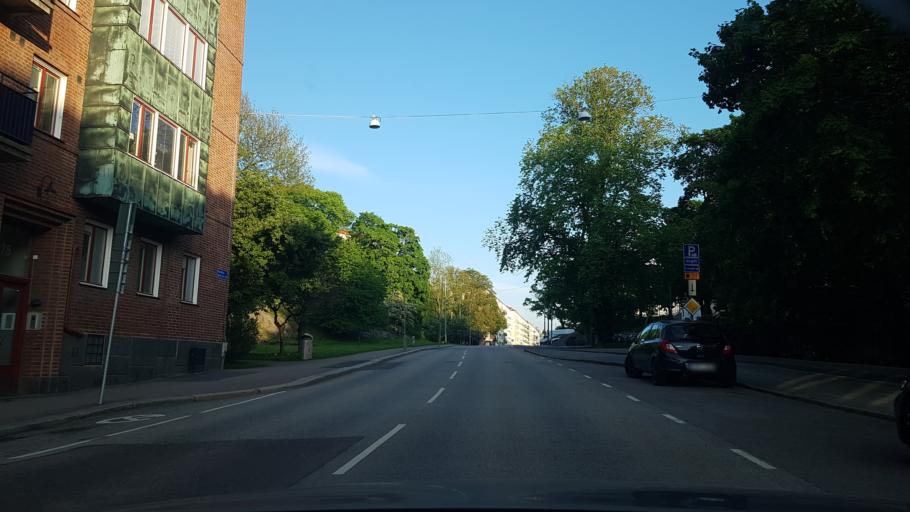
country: SE
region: Vaestra Goetaland
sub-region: Goteborg
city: Goeteborg
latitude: 57.6915
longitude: 11.9784
